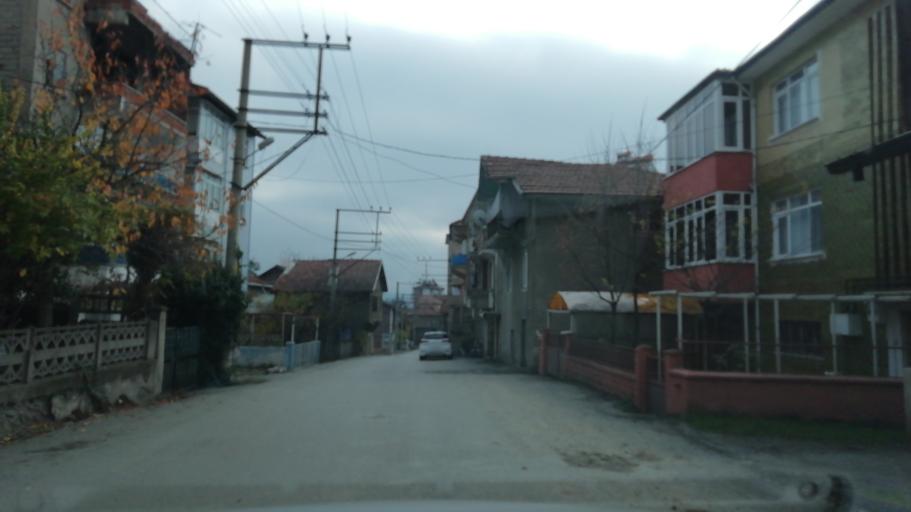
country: TR
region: Karabuk
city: Karabuk
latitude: 41.2219
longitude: 32.6268
